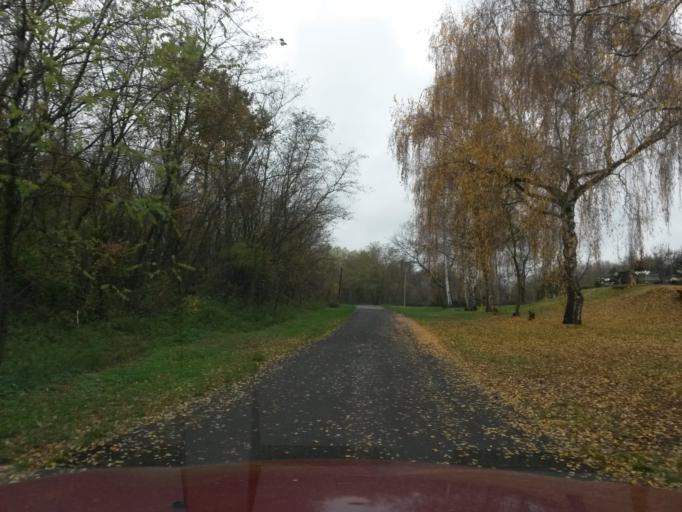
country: SK
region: Kosicky
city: Cierna nad Tisou
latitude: 48.5562
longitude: 21.9517
